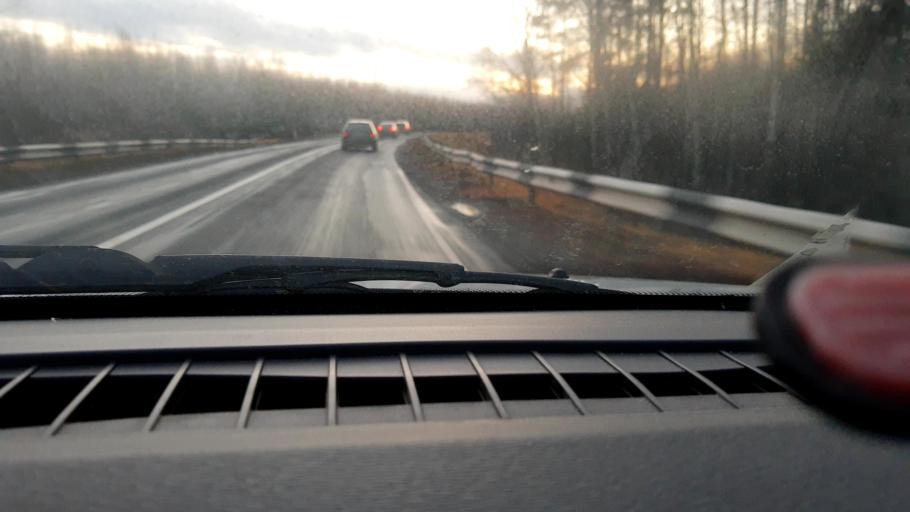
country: RU
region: Nizjnij Novgorod
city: Krasnyye Baki
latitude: 57.0988
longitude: 45.1778
